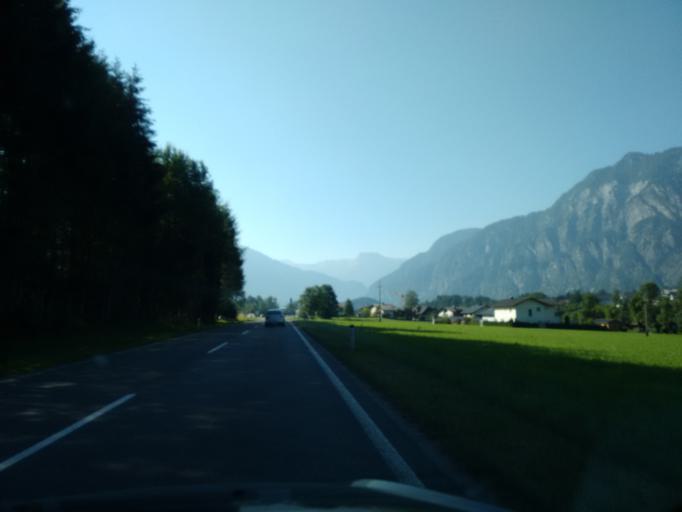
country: AT
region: Upper Austria
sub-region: Politischer Bezirk Gmunden
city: Bad Goisern
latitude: 47.6386
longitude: 13.6226
